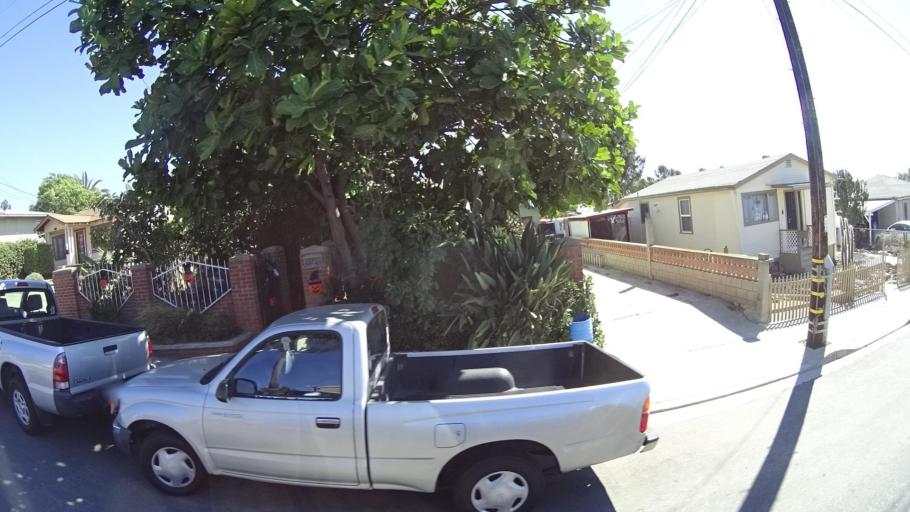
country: US
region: California
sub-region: San Diego County
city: National City
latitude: 32.6668
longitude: -117.0729
